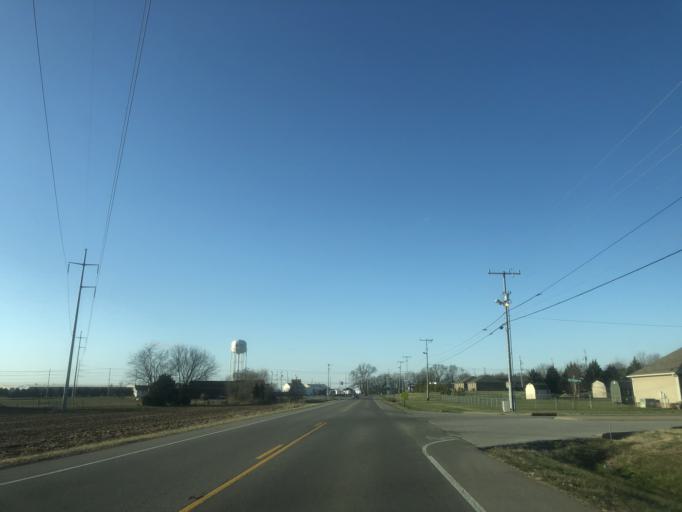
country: US
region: Tennessee
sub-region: Sumner County
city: Portland
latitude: 36.6304
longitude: -86.5618
